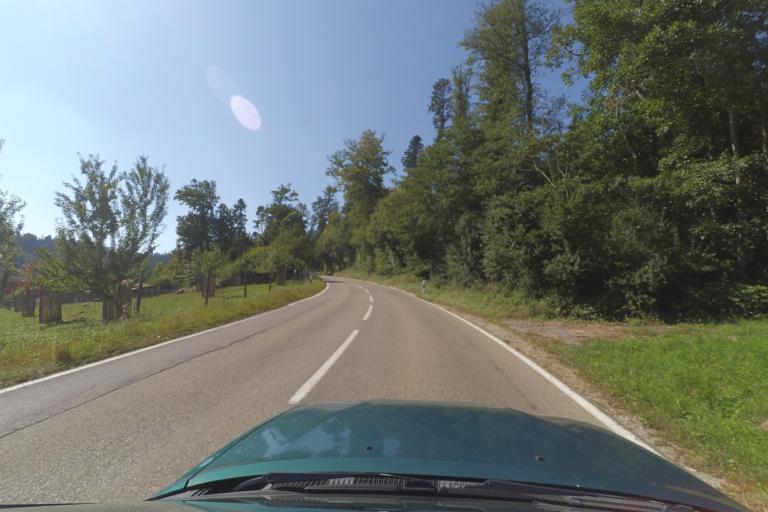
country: DE
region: Baden-Wuerttemberg
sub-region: Regierungsbezirk Stuttgart
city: Taferrot
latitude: 48.8533
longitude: 9.8344
